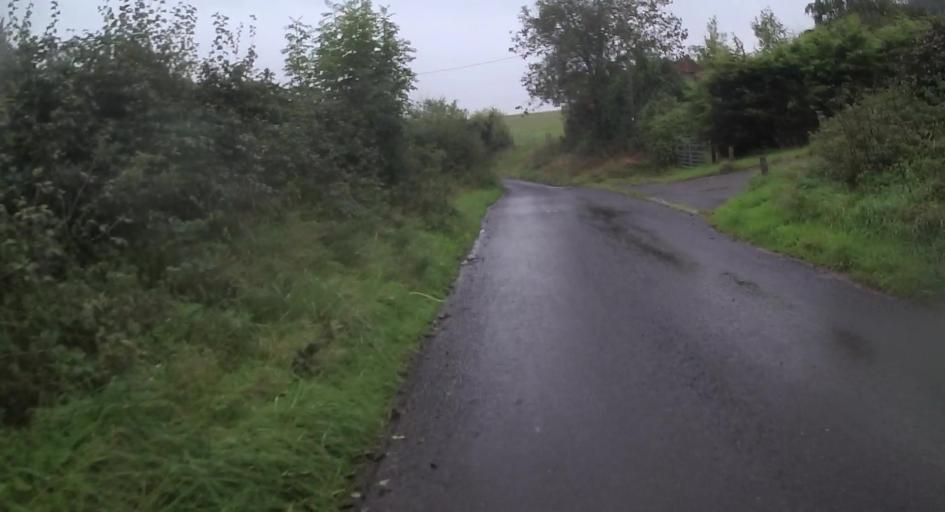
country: GB
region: England
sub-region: West Berkshire
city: Thatcham
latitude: 51.4054
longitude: -1.2104
